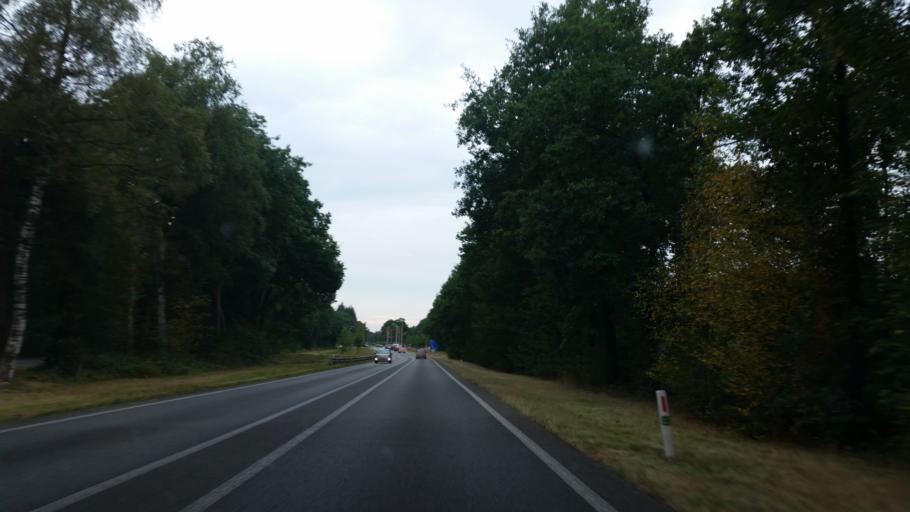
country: NL
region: Gelderland
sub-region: Gemeente Ede
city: Wekerom
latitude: 52.0685
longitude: 5.6940
